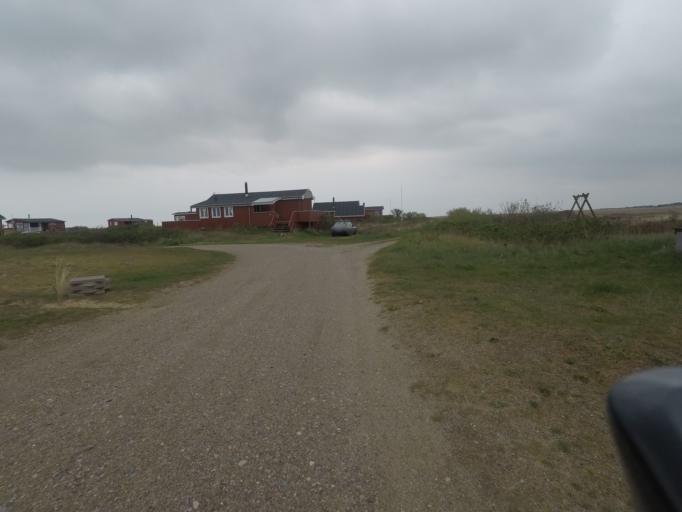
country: DE
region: Schleswig-Holstein
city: List
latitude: 55.1502
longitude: 8.4992
